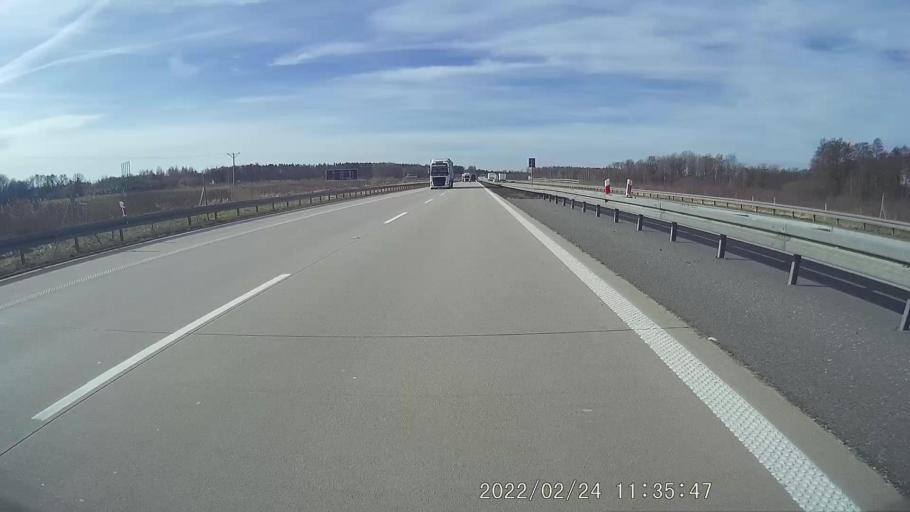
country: PL
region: Lower Silesian Voivodeship
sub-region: Powiat polkowicki
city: Przemkow
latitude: 51.5243
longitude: 15.7978
